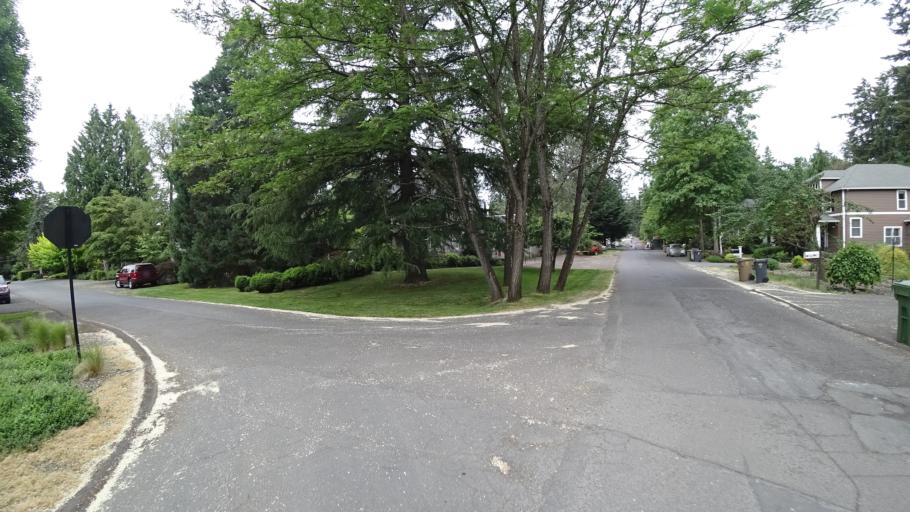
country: US
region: Oregon
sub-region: Clackamas County
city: Lake Oswego
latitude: 45.4265
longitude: -122.6703
